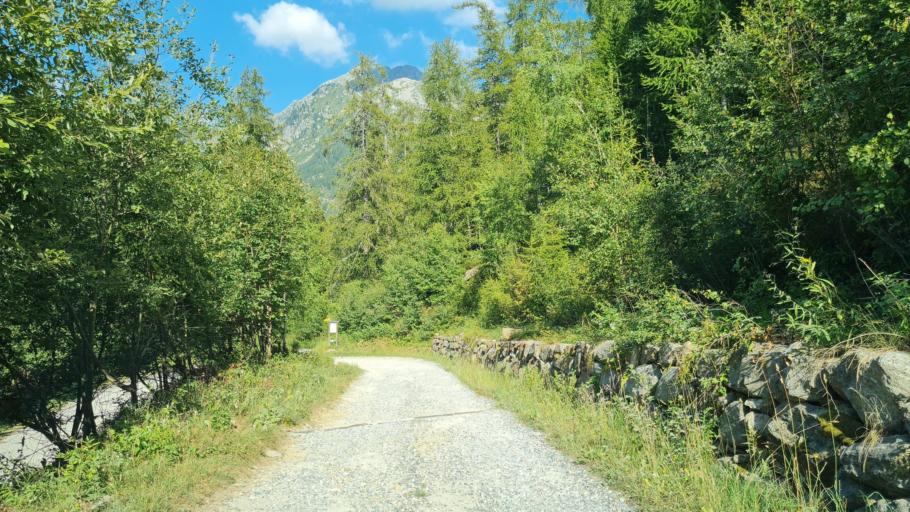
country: IT
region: Aosta Valley
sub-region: Valle d'Aosta
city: Fontainemore
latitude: 45.6303
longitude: 7.8692
